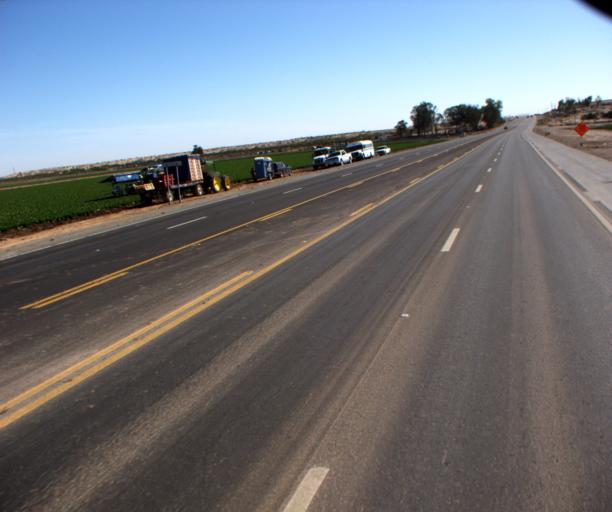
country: US
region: Arizona
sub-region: Yuma County
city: Somerton
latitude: 32.5967
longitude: -114.6825
